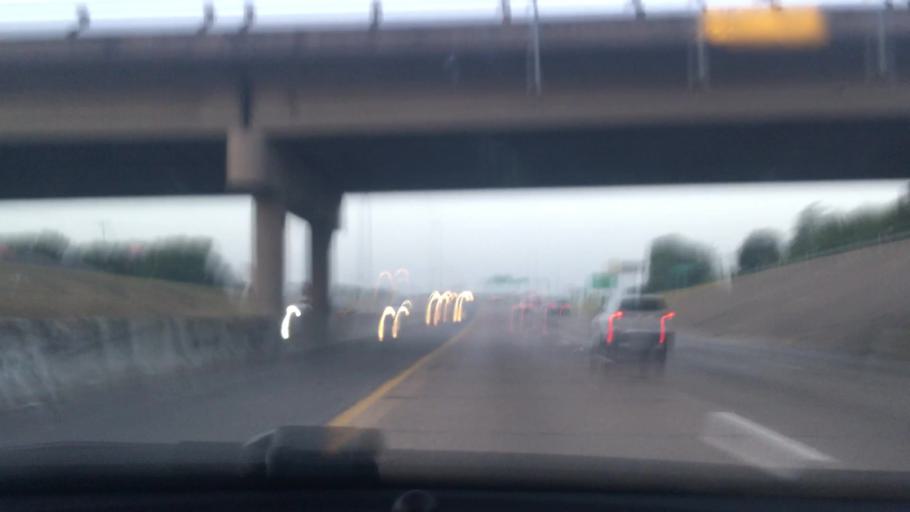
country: US
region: Texas
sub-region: Dallas County
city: DeSoto
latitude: 32.6542
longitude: -96.8233
